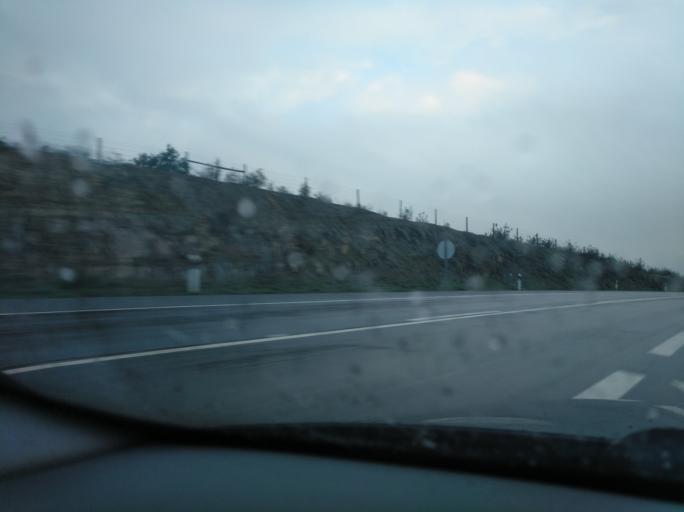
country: PT
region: Faro
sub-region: Alcoutim
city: Alcoutim
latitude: 37.3742
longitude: -7.5241
